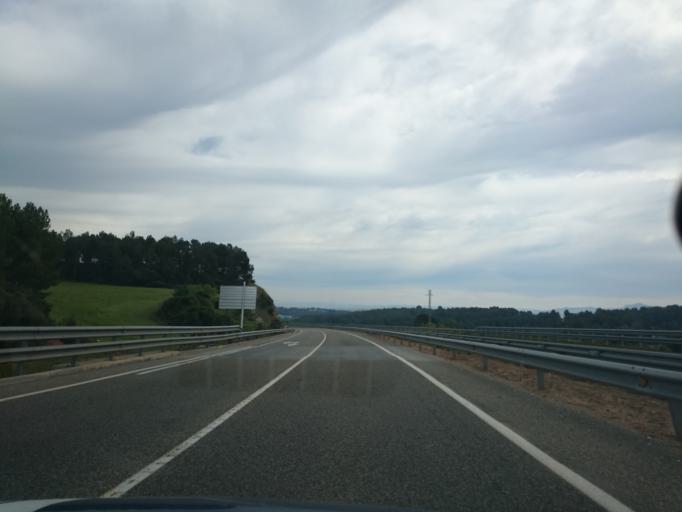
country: ES
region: Catalonia
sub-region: Provincia de Barcelona
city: Sant Salvador de Guardiola
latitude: 41.6899
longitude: 1.7758
